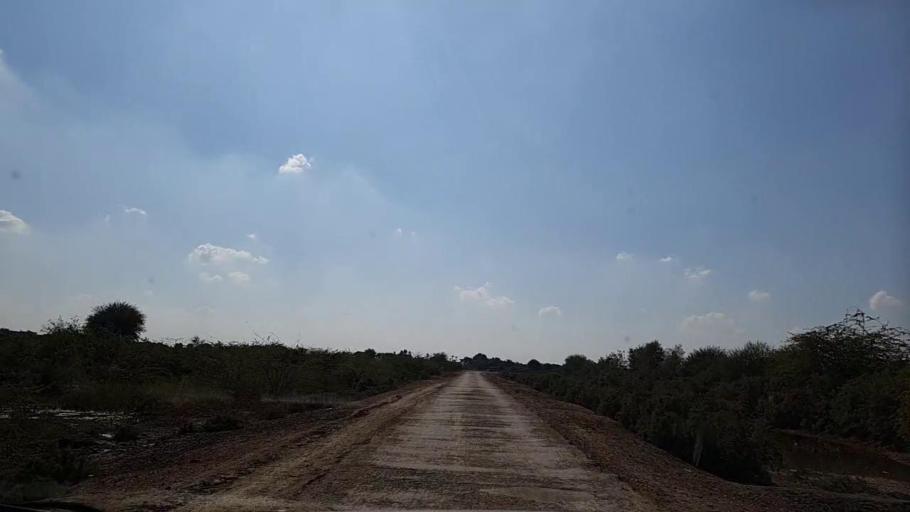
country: PK
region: Sindh
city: Pithoro
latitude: 25.6704
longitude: 69.4772
